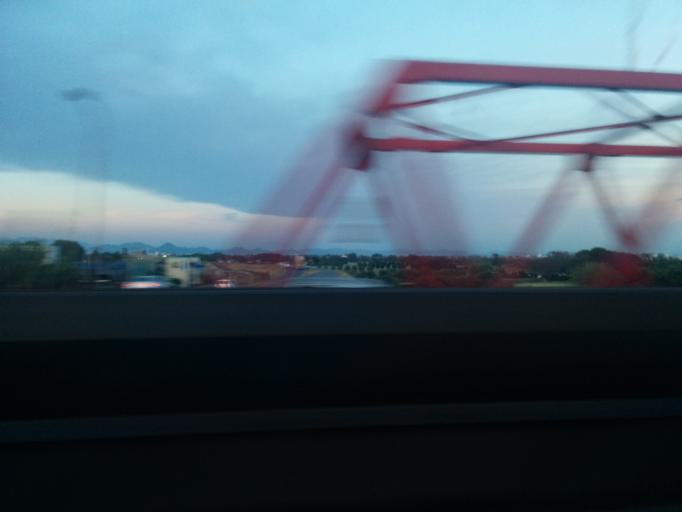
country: JP
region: Gifu
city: Ogaki
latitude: 35.3258
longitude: 136.6740
